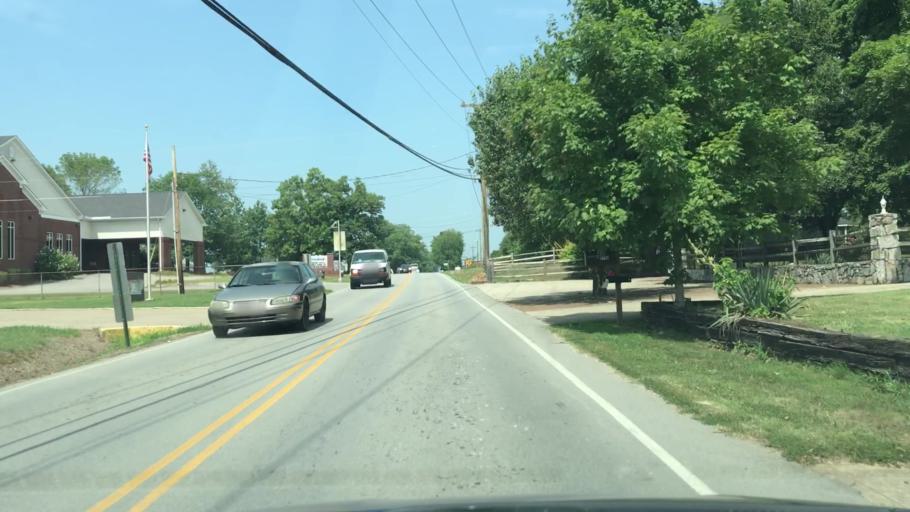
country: US
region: Tennessee
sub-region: Wilson County
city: Rural Hill
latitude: 36.1129
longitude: -86.4191
